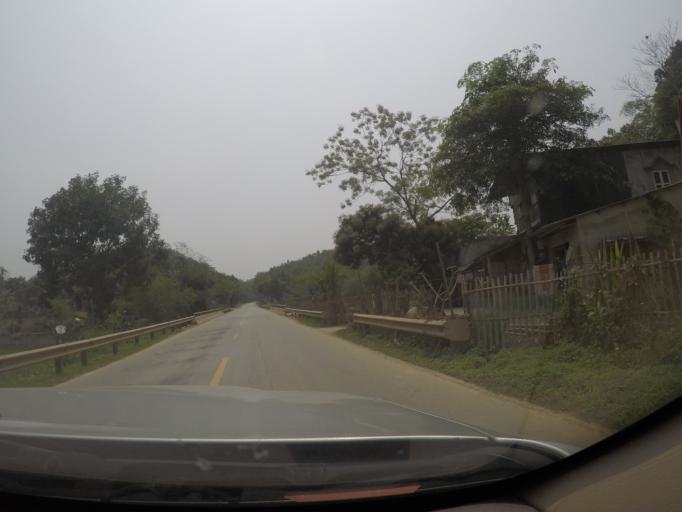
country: VN
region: Thanh Hoa
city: Thi Tran Thuong Xuan
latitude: 19.8485
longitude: 105.4040
